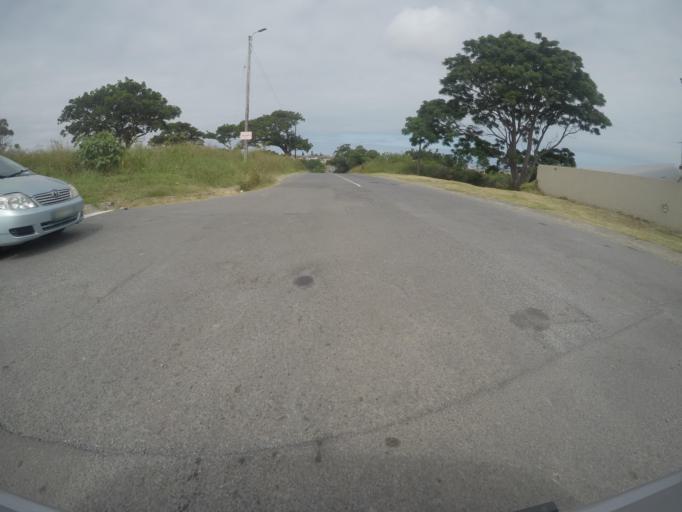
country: ZA
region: Eastern Cape
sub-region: Buffalo City Metropolitan Municipality
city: East London
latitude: -33.0022
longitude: 27.8795
